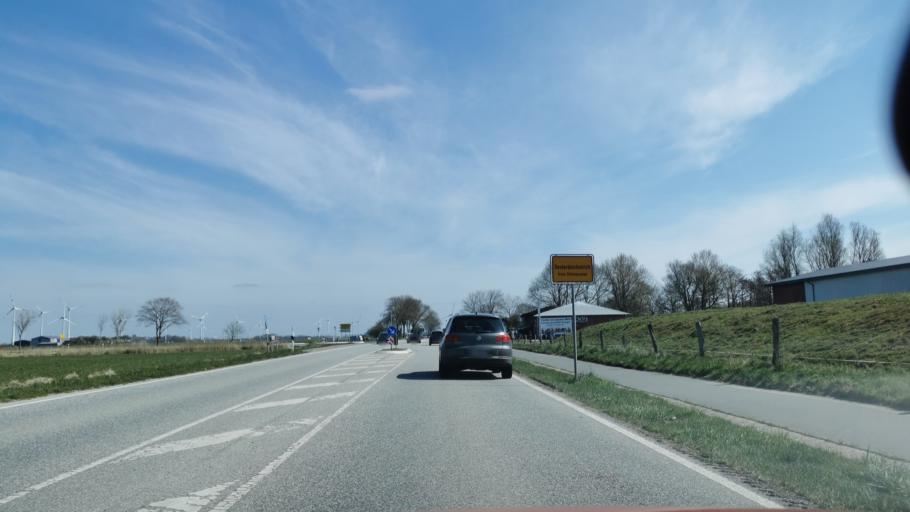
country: DE
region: Schleswig-Holstein
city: Oesterdeichstrich
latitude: 54.1591
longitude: 8.8990
